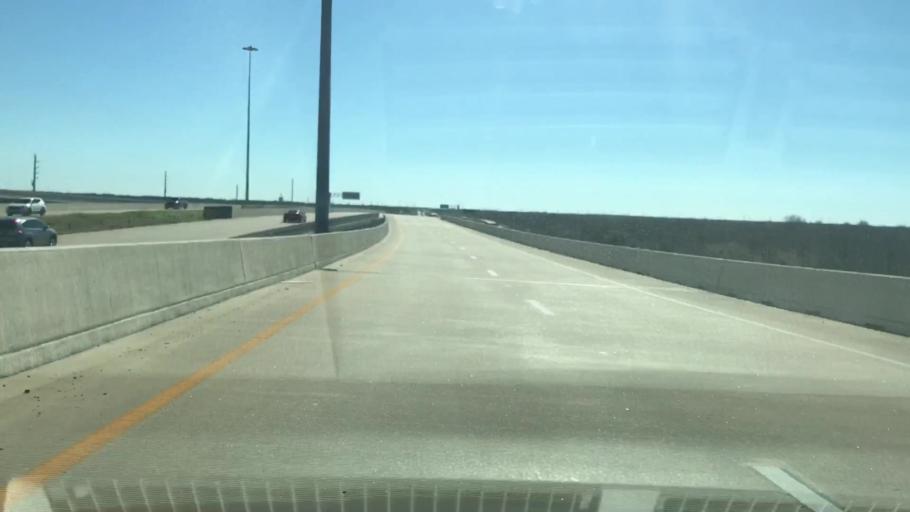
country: US
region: Texas
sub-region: Harris County
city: Cypress
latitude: 29.9942
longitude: -95.7692
